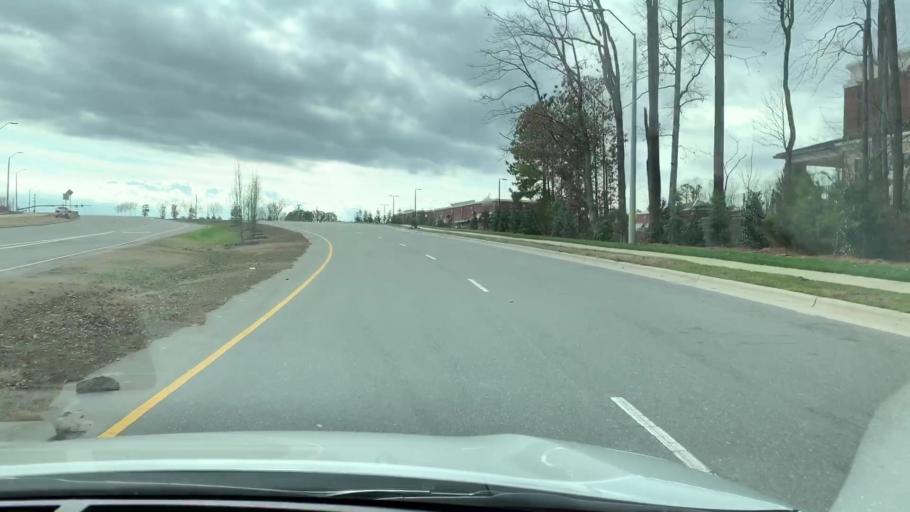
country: US
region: North Carolina
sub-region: Wake County
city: Green Level
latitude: 35.8252
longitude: -78.9024
